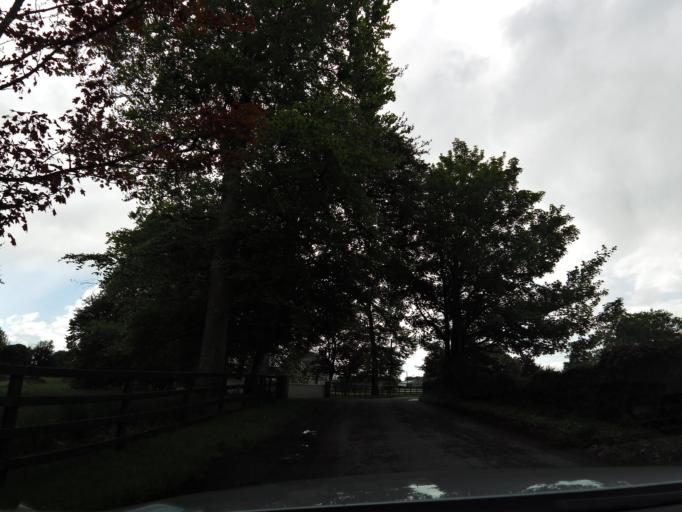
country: IE
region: Leinster
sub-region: Laois
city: Rathdowney
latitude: 52.7246
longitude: -7.5868
